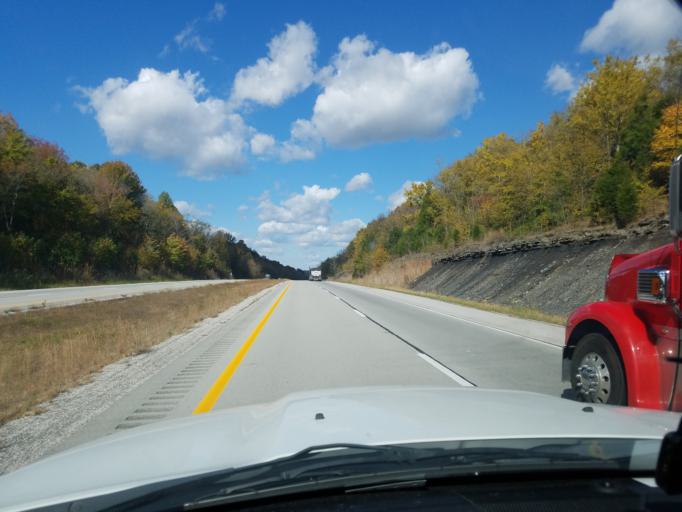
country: US
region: Kentucky
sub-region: Butler County
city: Morgantown
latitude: 37.2558
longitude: -86.7430
